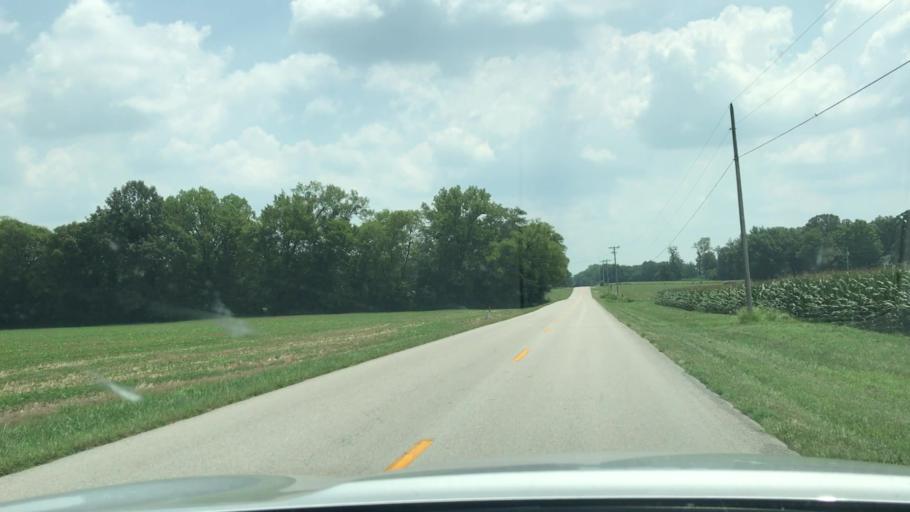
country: US
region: Kentucky
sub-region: Todd County
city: Elkton
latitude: 36.7659
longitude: -87.1100
